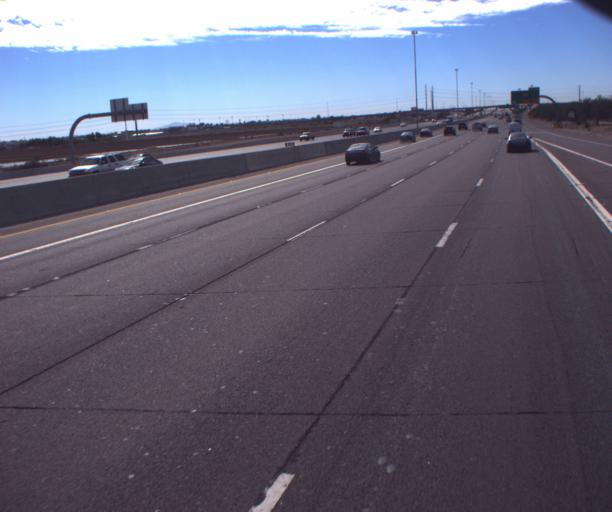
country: US
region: Arizona
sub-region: Maricopa County
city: Tempe
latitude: 33.4476
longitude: -111.8910
